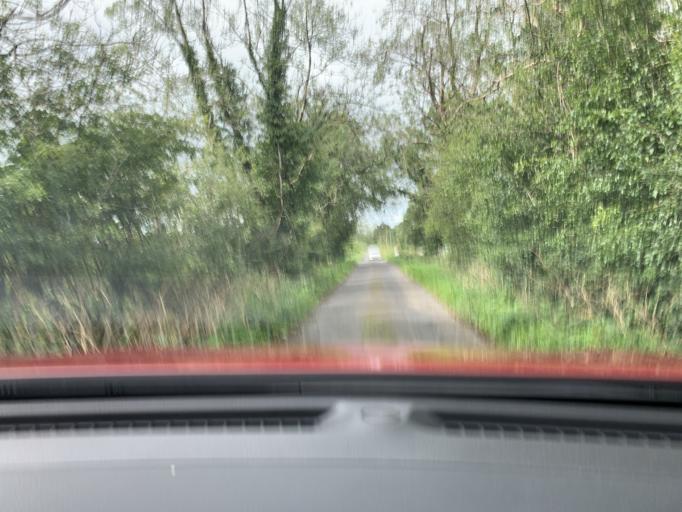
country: IE
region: Connaught
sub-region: Sligo
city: Collooney
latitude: 54.1573
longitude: -8.4282
